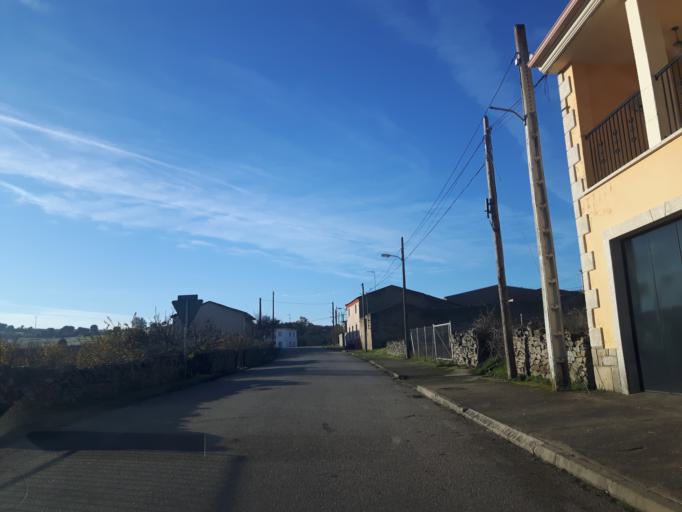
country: ES
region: Castille and Leon
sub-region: Provincia de Salamanca
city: Cerralbo
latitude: 40.9720
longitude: -6.5882
